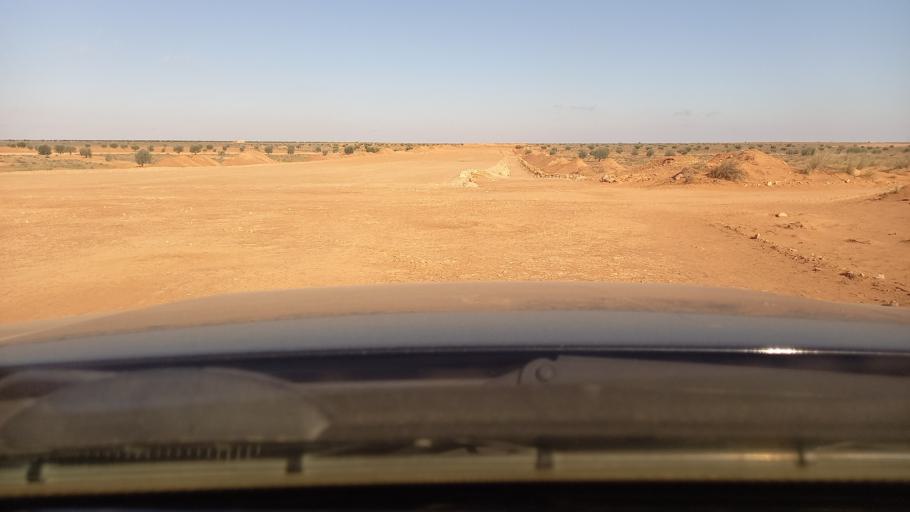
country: TN
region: Madanin
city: Medenine
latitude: 33.1754
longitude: 10.5282
